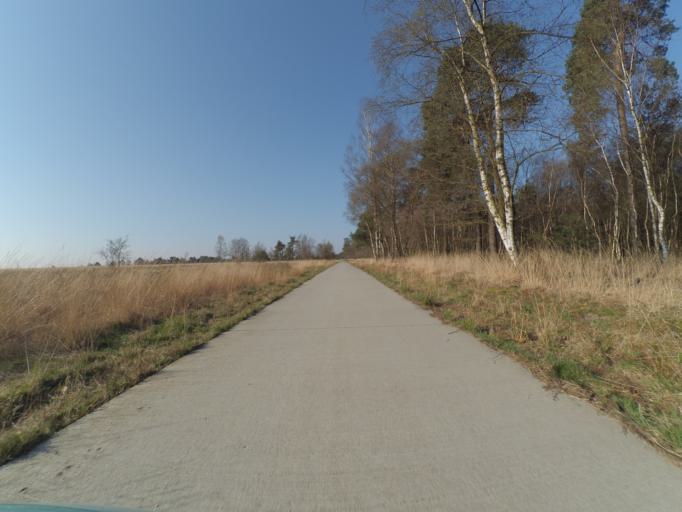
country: NL
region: Gelderland
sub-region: Gemeente Ede
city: Otterlo
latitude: 52.0973
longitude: 5.8588
